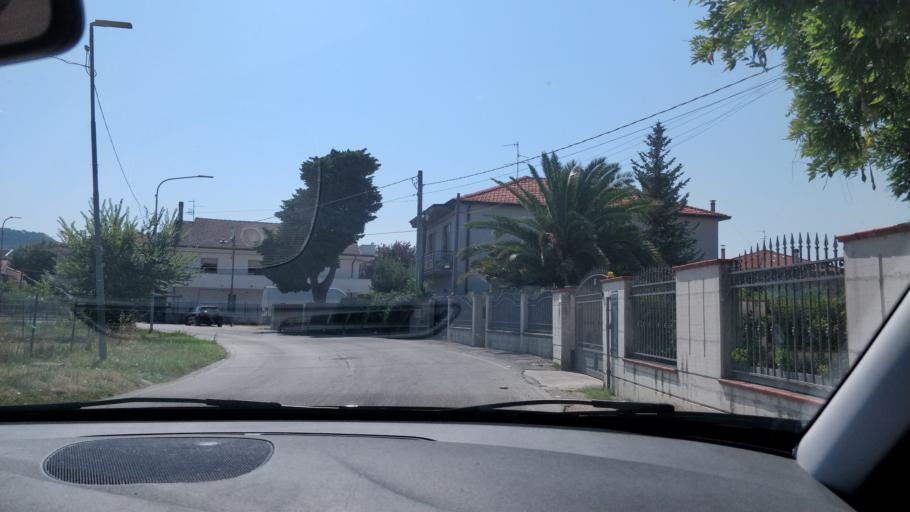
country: IT
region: Abruzzo
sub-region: Provincia di Chieti
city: Sambuceto
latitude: 42.4208
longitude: 14.1765
